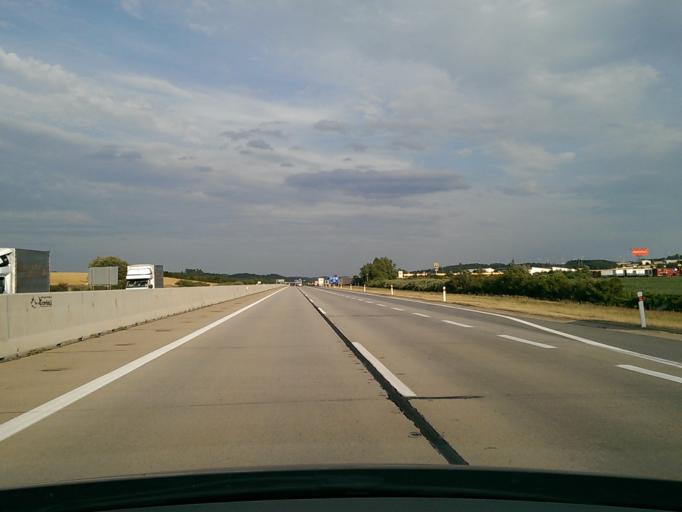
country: CZ
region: Vysocina
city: Merin
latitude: 49.3801
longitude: 15.9415
